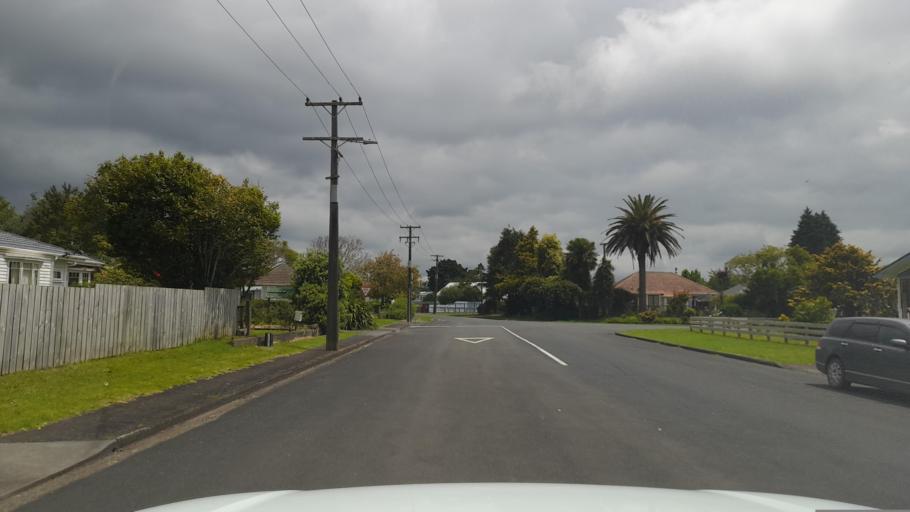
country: NZ
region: Northland
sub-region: Far North District
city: Waimate North
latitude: -35.4058
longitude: 173.8061
